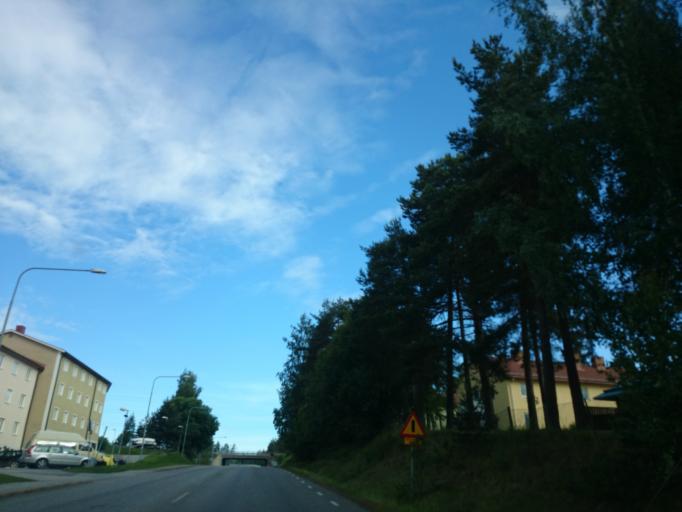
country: SE
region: Vaesternorrland
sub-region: Timra Kommun
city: Timra
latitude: 62.4903
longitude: 17.3297
